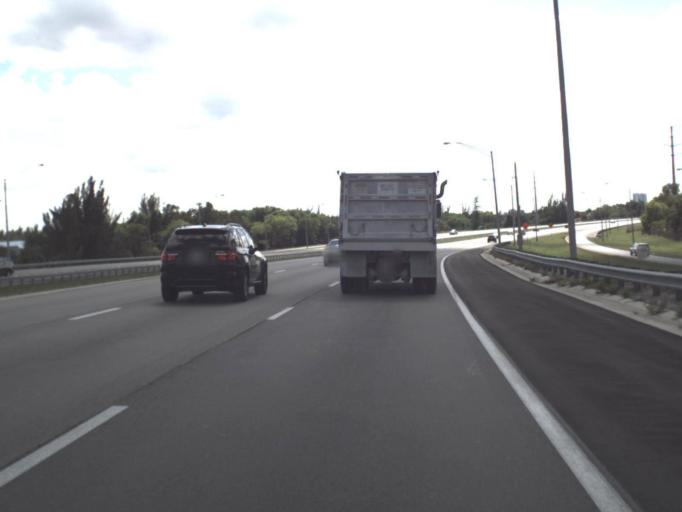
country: US
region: Florida
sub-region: Broward County
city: Tamarac
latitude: 26.1918
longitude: -80.2954
